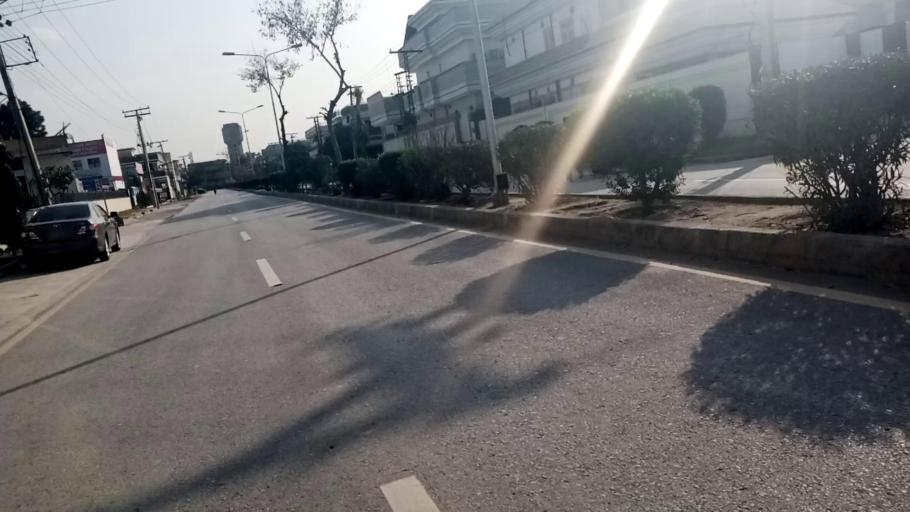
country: PK
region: Khyber Pakhtunkhwa
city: Peshawar
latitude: 33.9878
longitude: 71.4456
